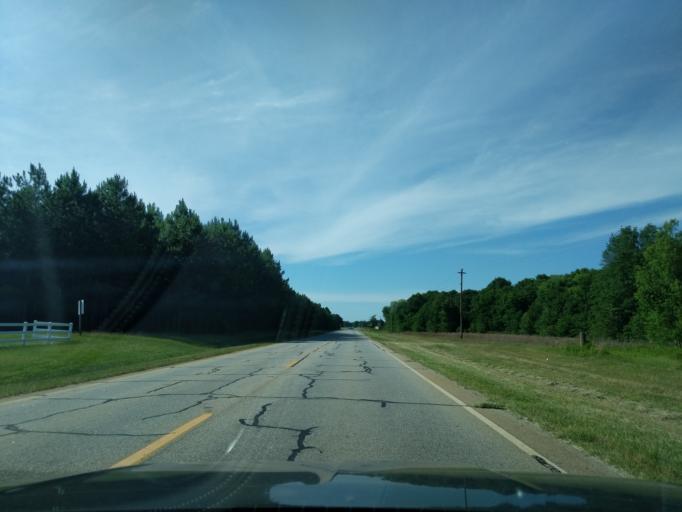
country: US
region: Georgia
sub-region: Jefferson County
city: Wrens
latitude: 33.2243
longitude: -82.3793
